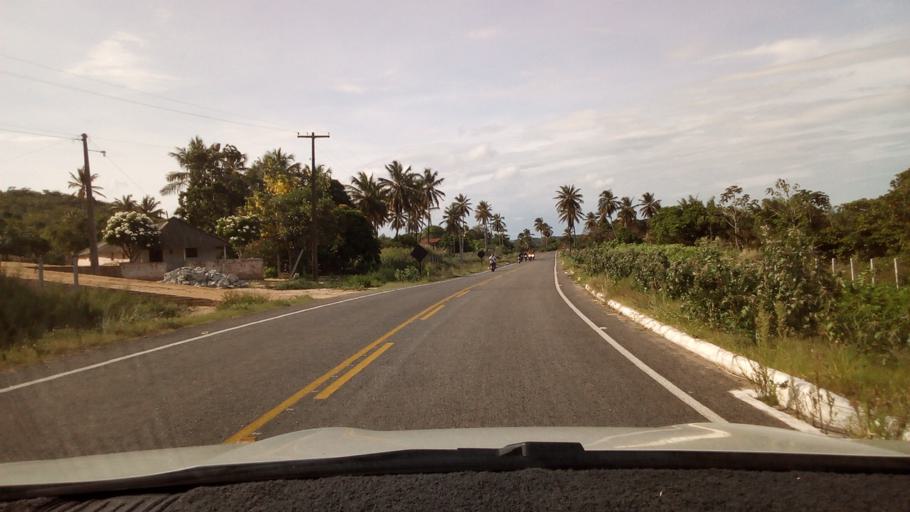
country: BR
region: Paraiba
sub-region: Cabedelo
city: Cabedelo
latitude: -7.0147
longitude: -34.8783
